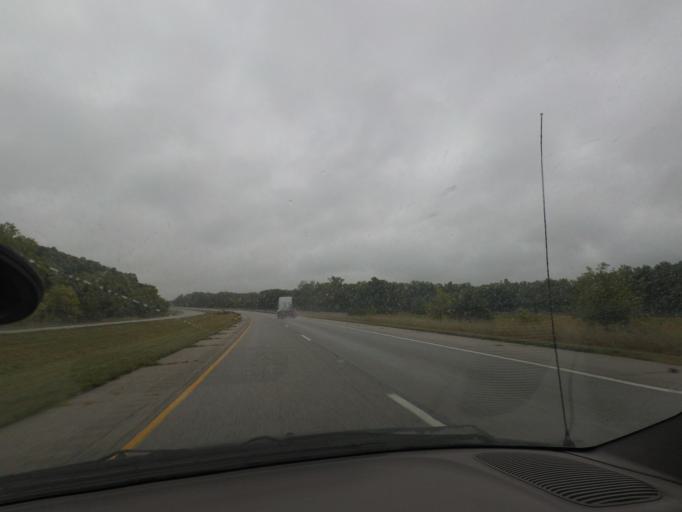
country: US
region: Illinois
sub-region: Pike County
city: Barry
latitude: 39.7133
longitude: -91.1031
